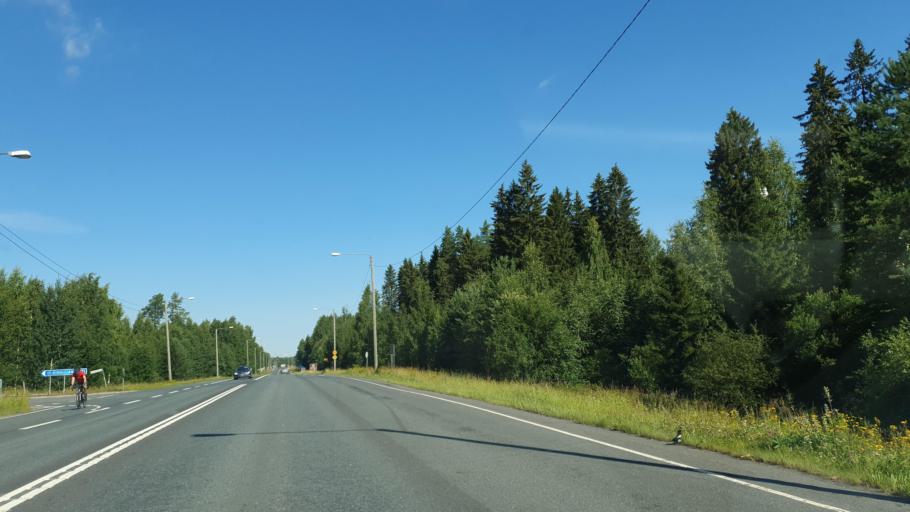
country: FI
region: Northern Savo
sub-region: Kuopio
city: Siilinjaervi
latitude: 63.1948
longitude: 27.5407
